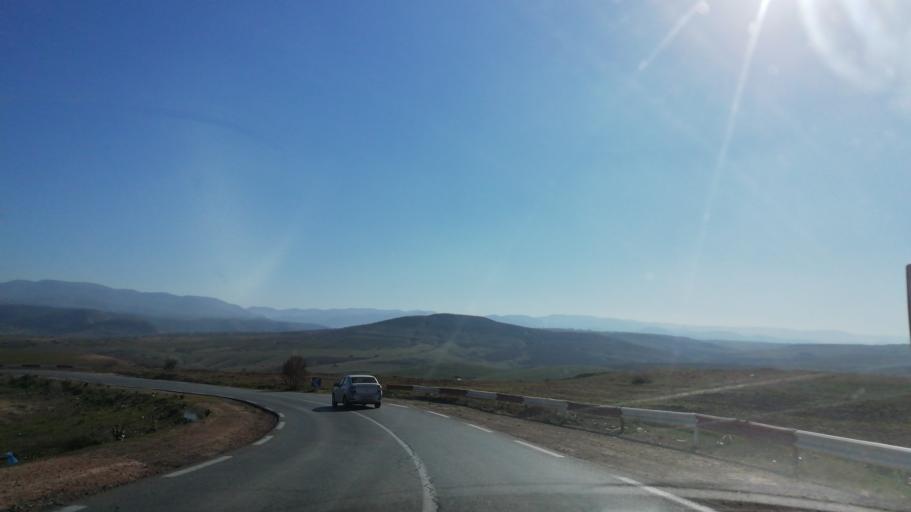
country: DZ
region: Tlemcen
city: Nedroma
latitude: 34.8308
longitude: -1.6751
